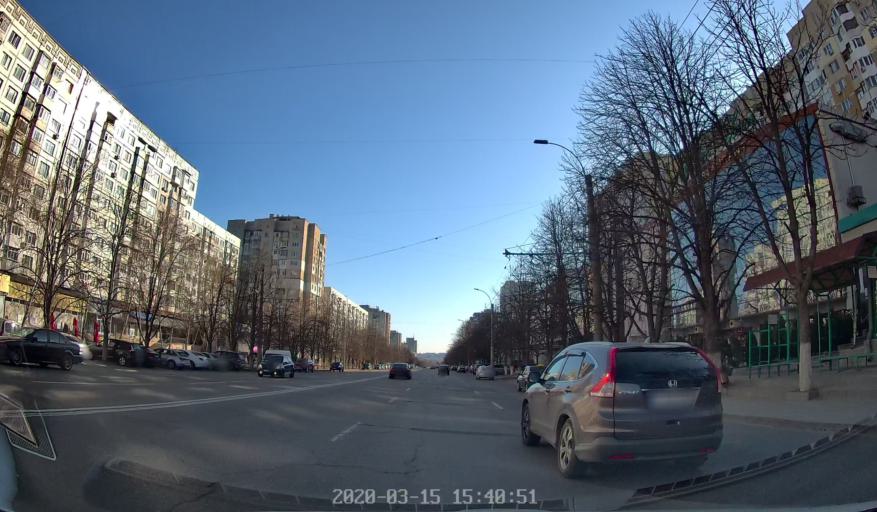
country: MD
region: Chisinau
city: Stauceni
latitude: 47.0547
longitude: 28.8652
